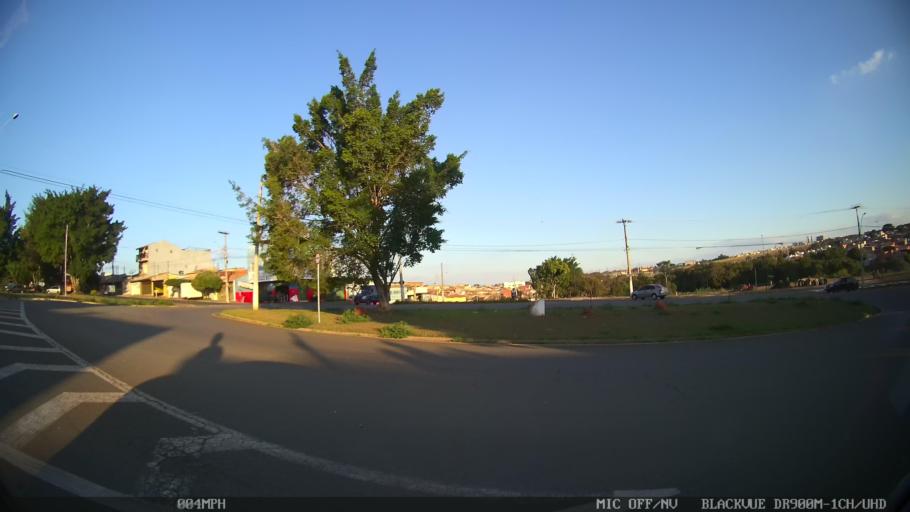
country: BR
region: Sao Paulo
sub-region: Santa Barbara D'Oeste
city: Santa Barbara d'Oeste
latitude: -22.7348
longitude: -47.3912
